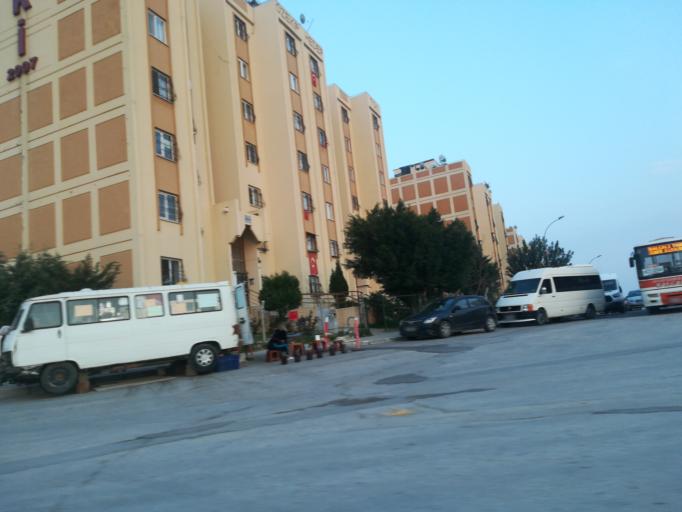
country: TR
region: Adana
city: Adana
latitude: 37.0725
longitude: 35.4077
